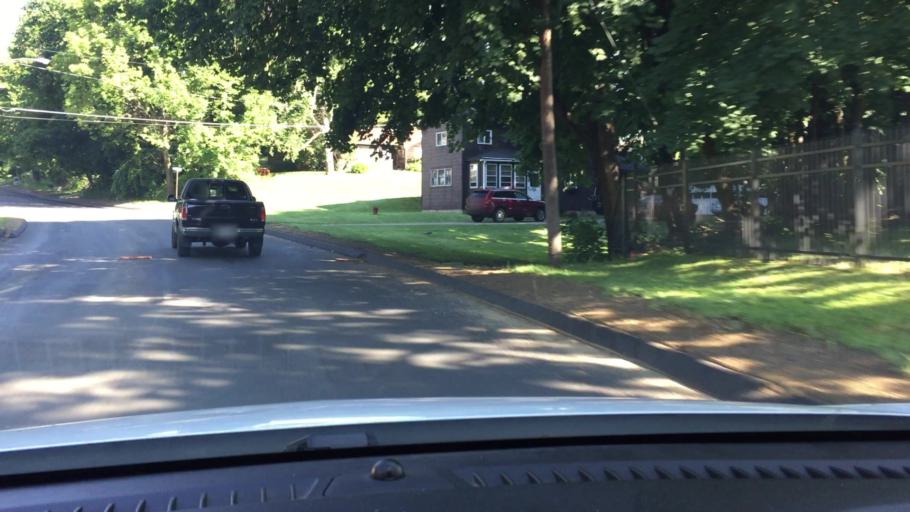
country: US
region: Massachusetts
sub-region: Berkshire County
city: Pittsfield
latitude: 42.4732
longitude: -73.2600
